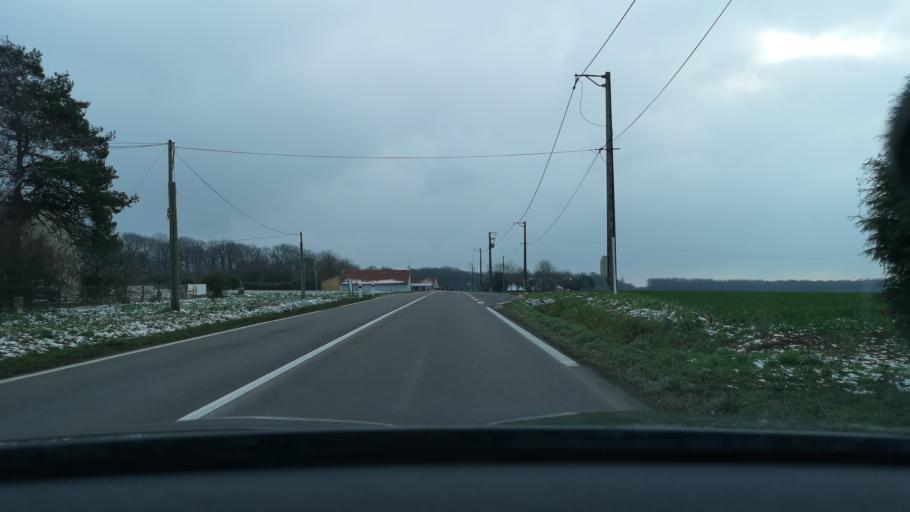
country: FR
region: Bourgogne
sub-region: Departement de Saone-et-Loire
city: Ouroux-sur-Saone
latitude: 46.7708
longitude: 4.9750
